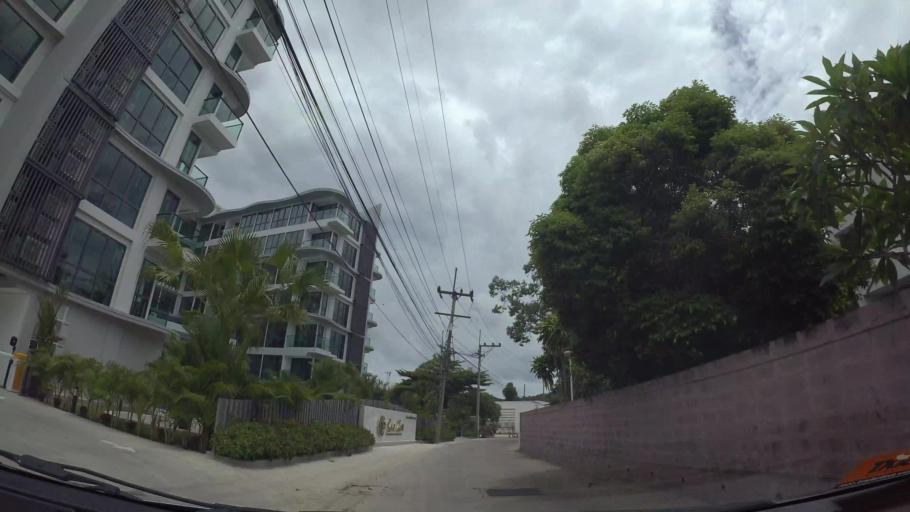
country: TH
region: Chon Buri
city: Sattahip
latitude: 12.7600
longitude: 100.8830
